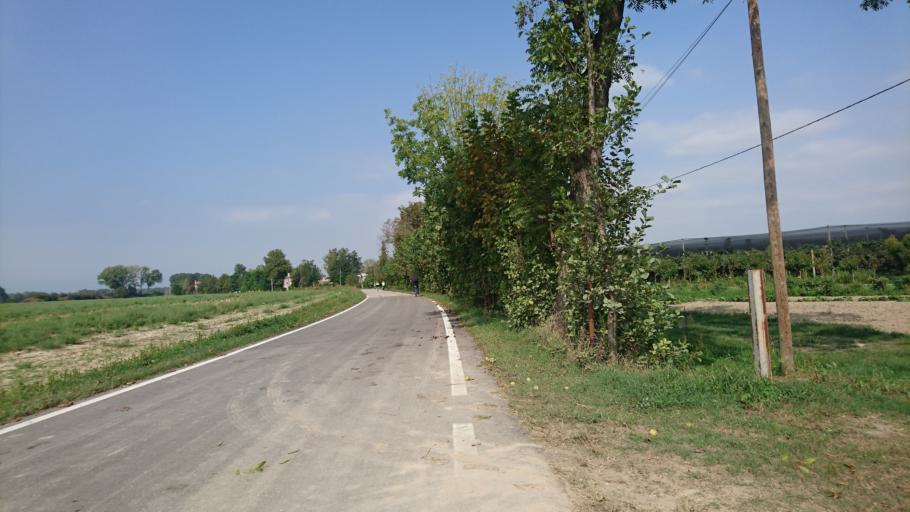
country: IT
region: Veneto
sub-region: Provincia di Padova
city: Piazzola sul Brenta
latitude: 45.5723
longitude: 11.7718
